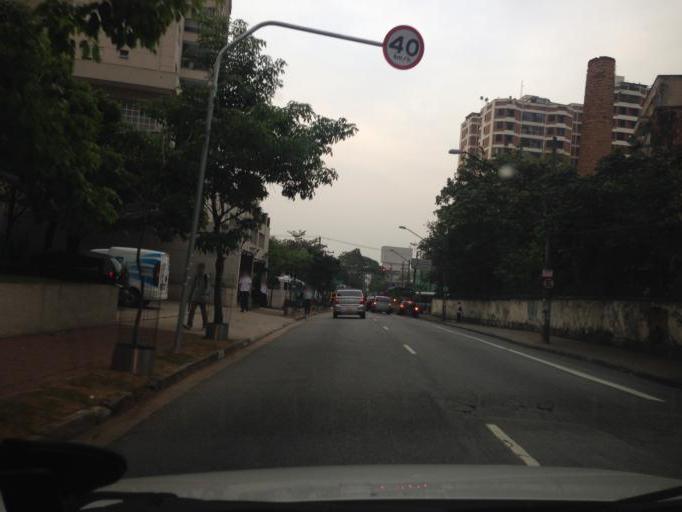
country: BR
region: Sao Paulo
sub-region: Sao Paulo
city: Sao Paulo
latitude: -23.5246
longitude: -46.7021
